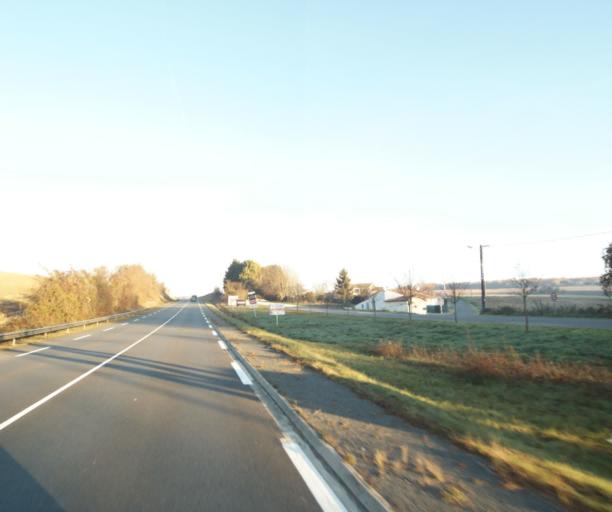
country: FR
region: Poitou-Charentes
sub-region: Departement de la Charente-Maritime
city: Cherac
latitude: 45.7190
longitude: -0.4950
